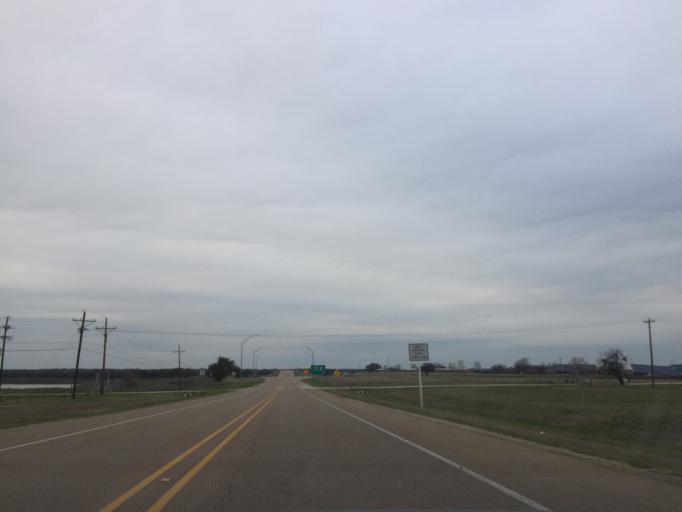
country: US
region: Texas
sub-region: Coryell County
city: Gatesville
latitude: 31.4796
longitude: -97.7273
